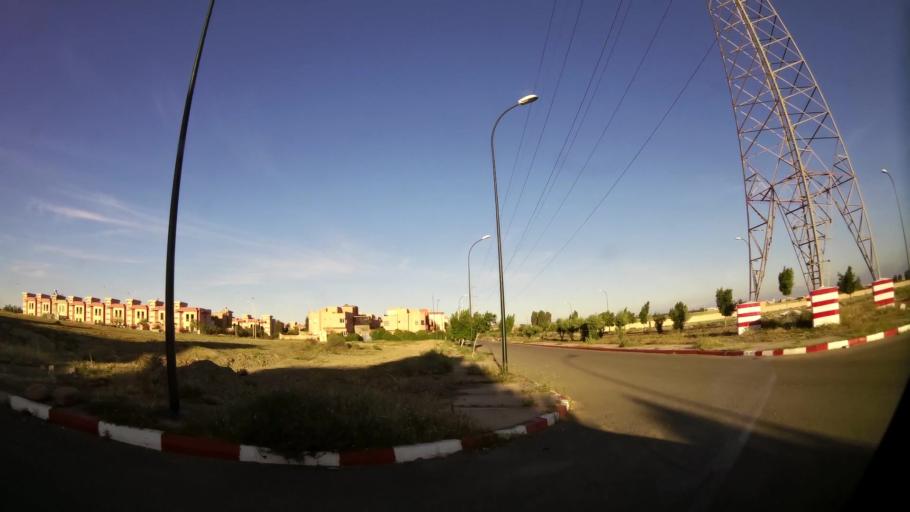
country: MA
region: Marrakech-Tensift-Al Haouz
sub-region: Marrakech
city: Marrakesh
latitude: 31.7430
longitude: -8.1148
